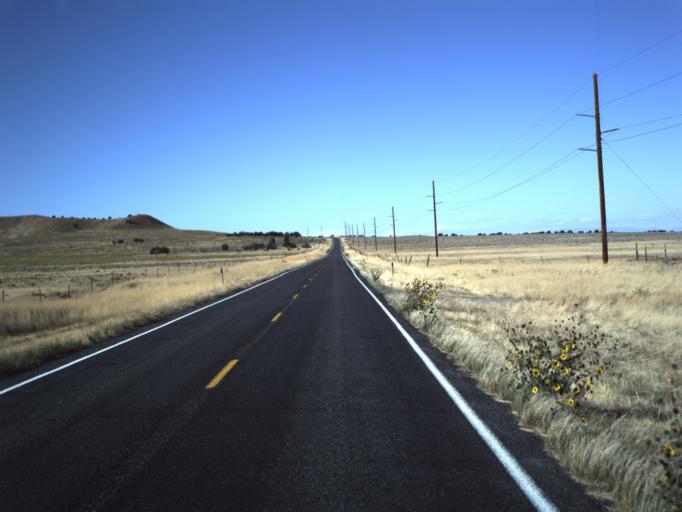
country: US
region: Utah
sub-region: Millard County
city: Delta
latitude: 39.4602
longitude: -112.2914
